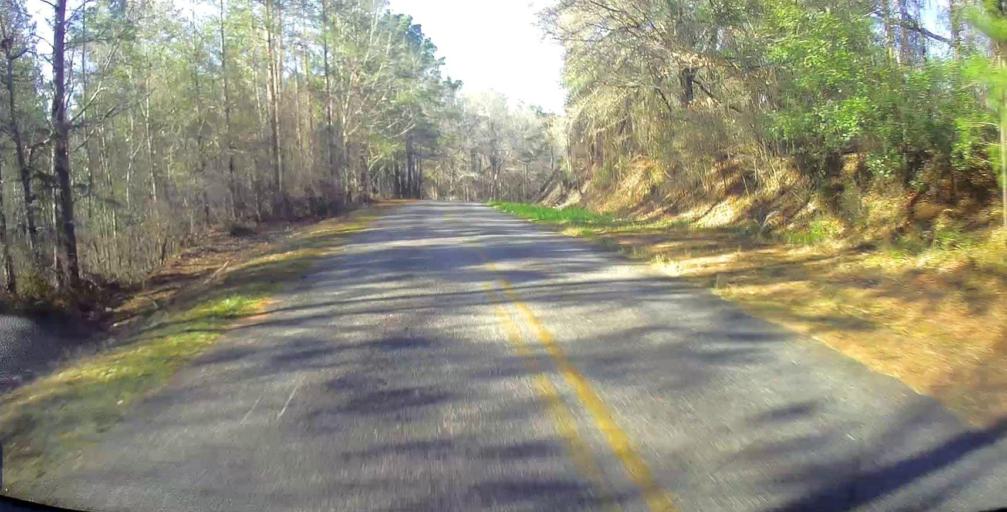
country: US
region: Georgia
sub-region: Macon County
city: Marshallville
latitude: 32.4721
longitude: -83.9517
